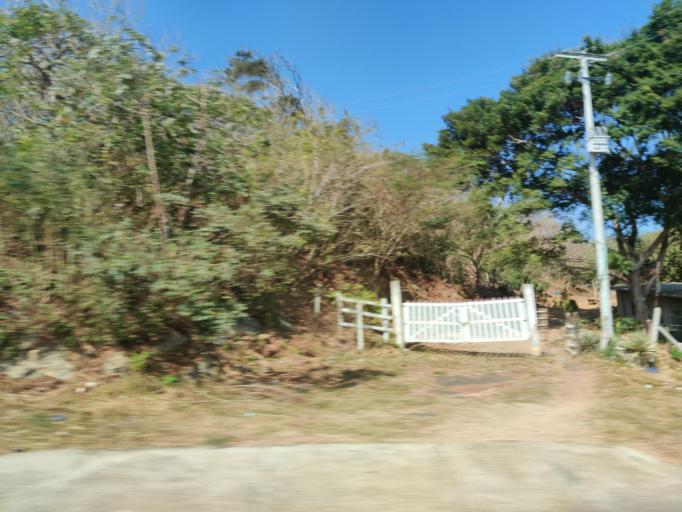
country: CO
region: Atlantico
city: Puerto Colombia
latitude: 10.9538
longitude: -75.0040
